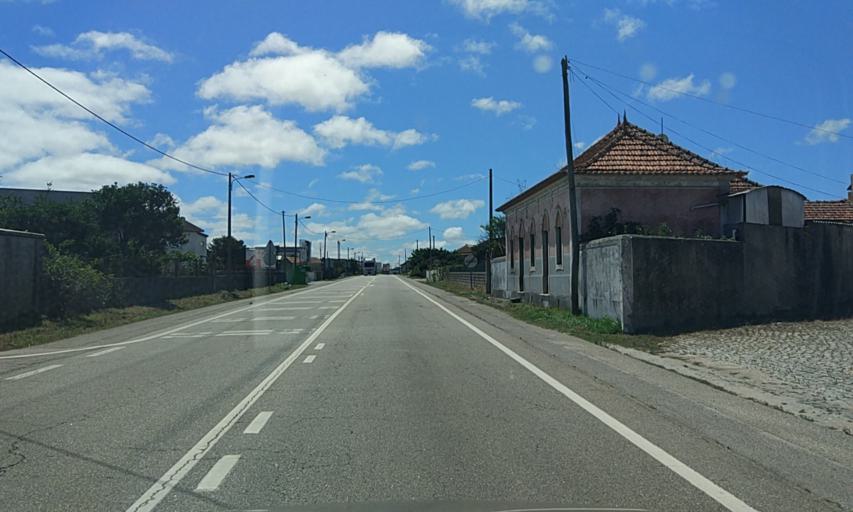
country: PT
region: Aveiro
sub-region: Vagos
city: Vagos
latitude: 40.4884
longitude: -8.6872
